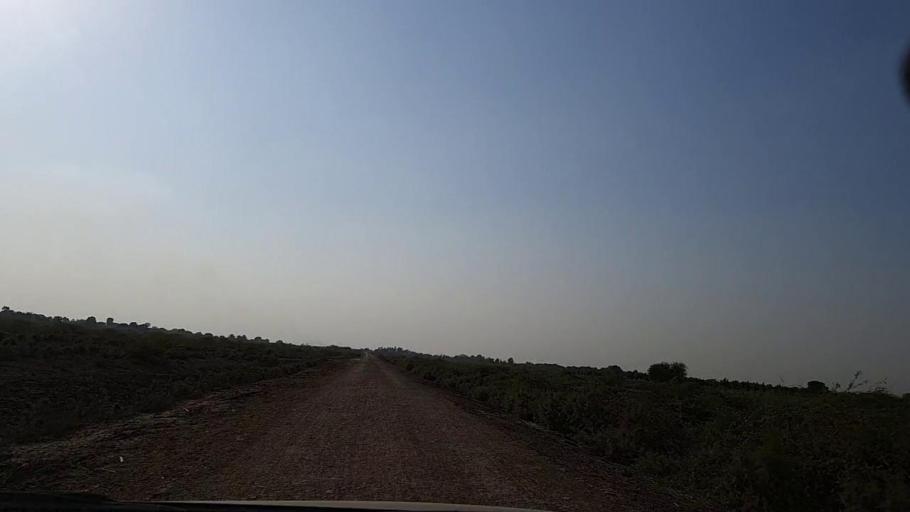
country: PK
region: Sindh
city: Mirwah Gorchani
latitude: 25.2240
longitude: 68.9711
